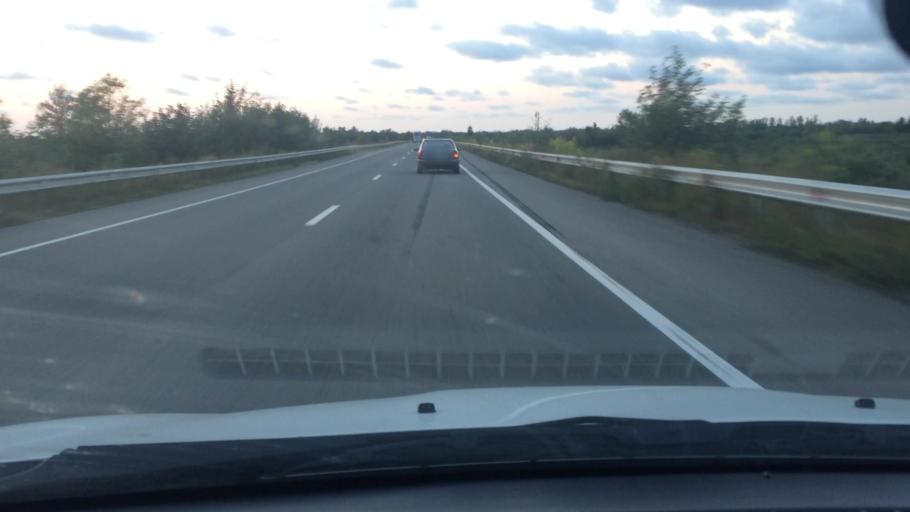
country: GE
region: Ajaria
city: Ochkhamuri
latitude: 41.9053
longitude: 41.7888
